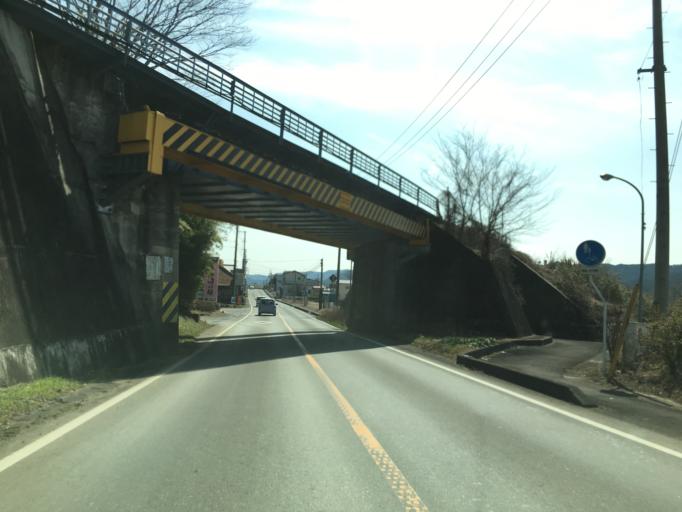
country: JP
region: Ibaraki
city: Daigo
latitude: 36.9158
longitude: 140.4168
